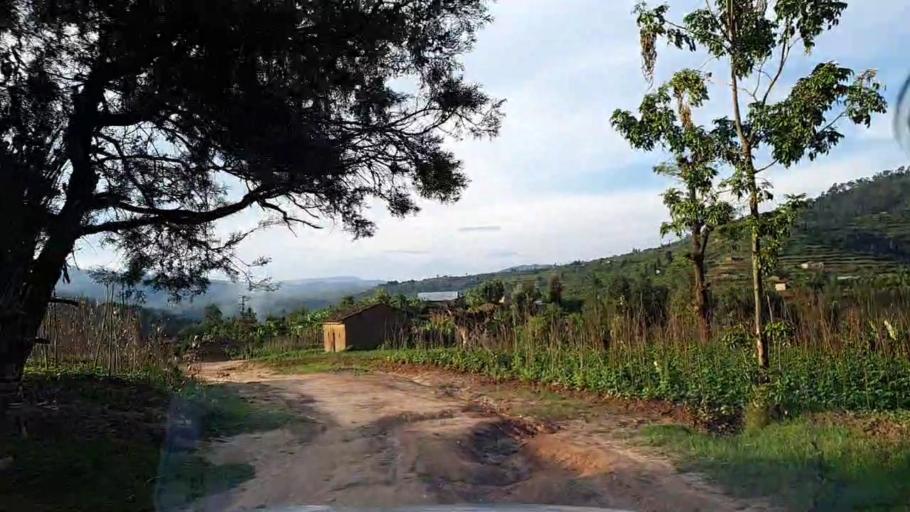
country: RW
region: Southern Province
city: Gikongoro
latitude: -2.4011
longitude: 29.5554
